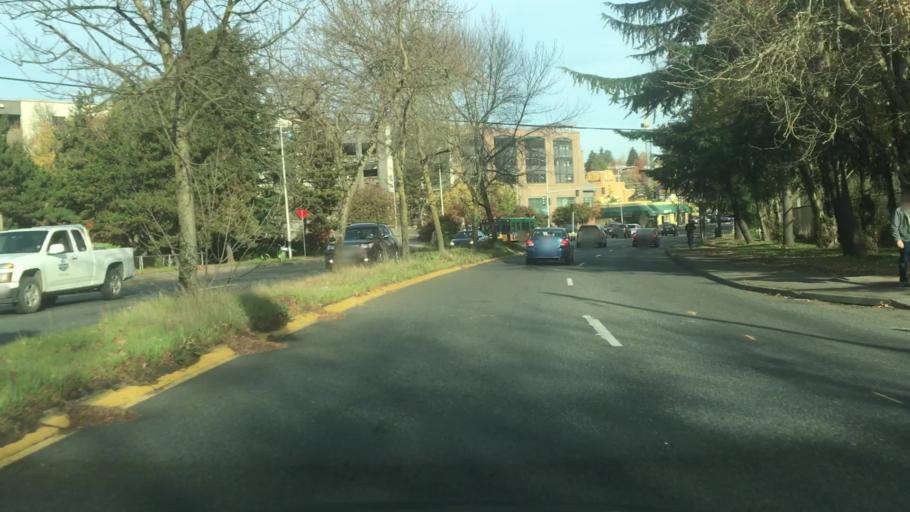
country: US
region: Washington
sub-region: King County
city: Seattle
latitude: 47.6567
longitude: -122.3036
